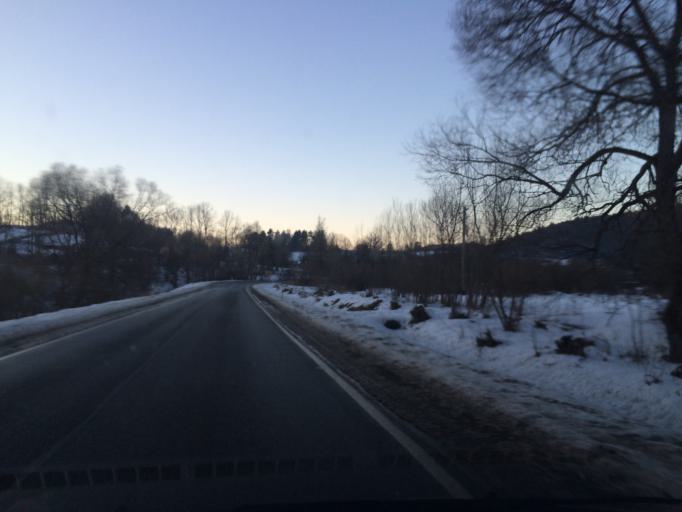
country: PL
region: Subcarpathian Voivodeship
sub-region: Powiat bieszczadzki
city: Czarna
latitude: 49.3825
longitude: 22.6389
